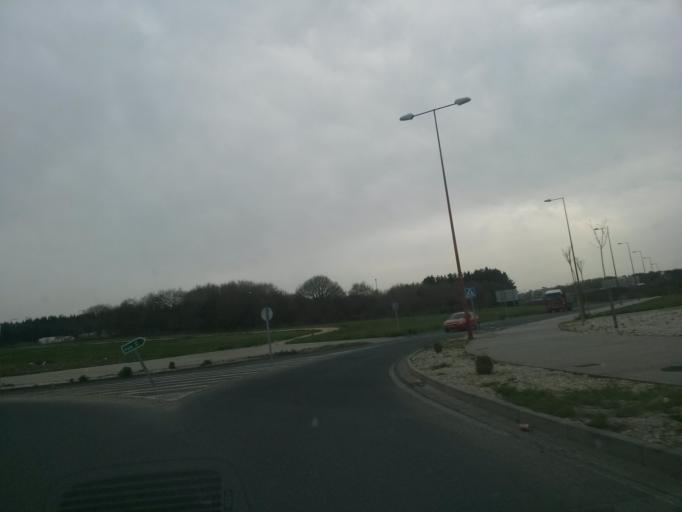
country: ES
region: Galicia
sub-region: Provincia de Lugo
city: Lugo
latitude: 43.0382
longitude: -7.5546
